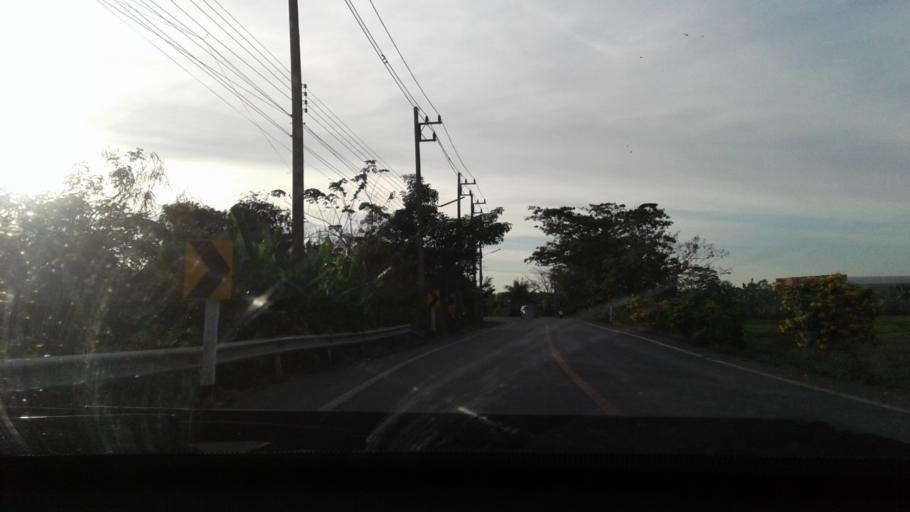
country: TH
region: Nonthaburi
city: Sai Noi
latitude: 13.8989
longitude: 100.2403
